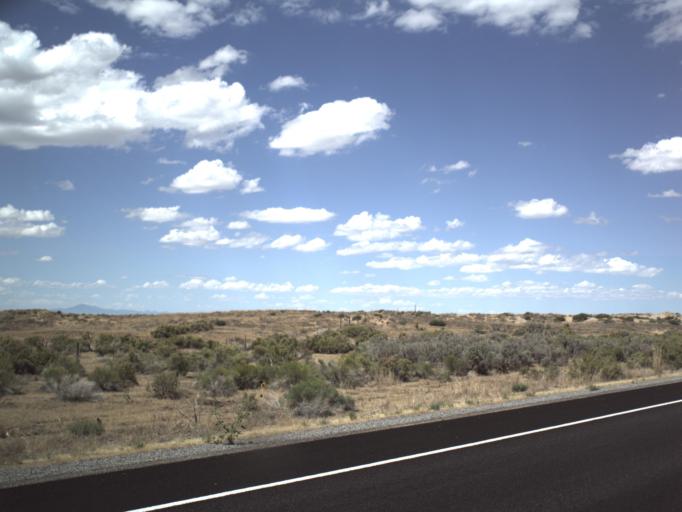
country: US
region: Utah
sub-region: Millard County
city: Fillmore
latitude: 39.1298
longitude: -112.3602
